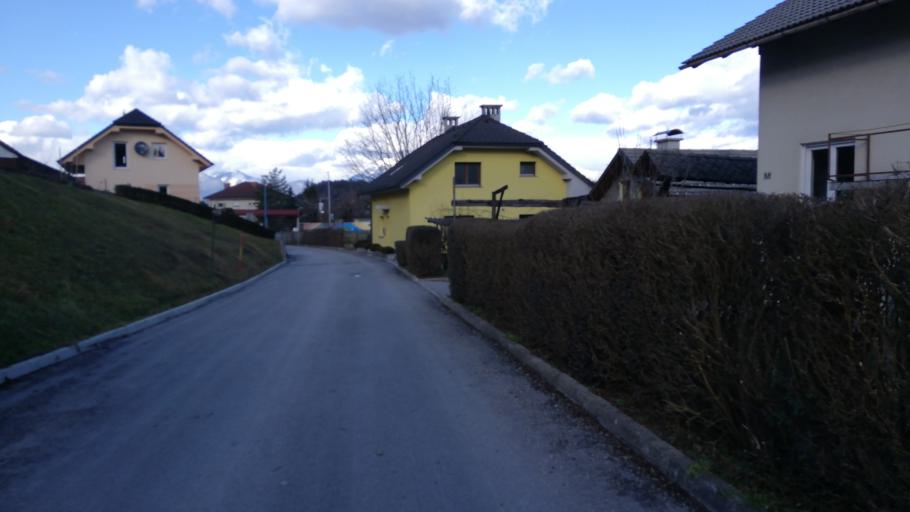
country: SI
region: Medvode
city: Medvode
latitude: 46.1312
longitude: 14.4110
